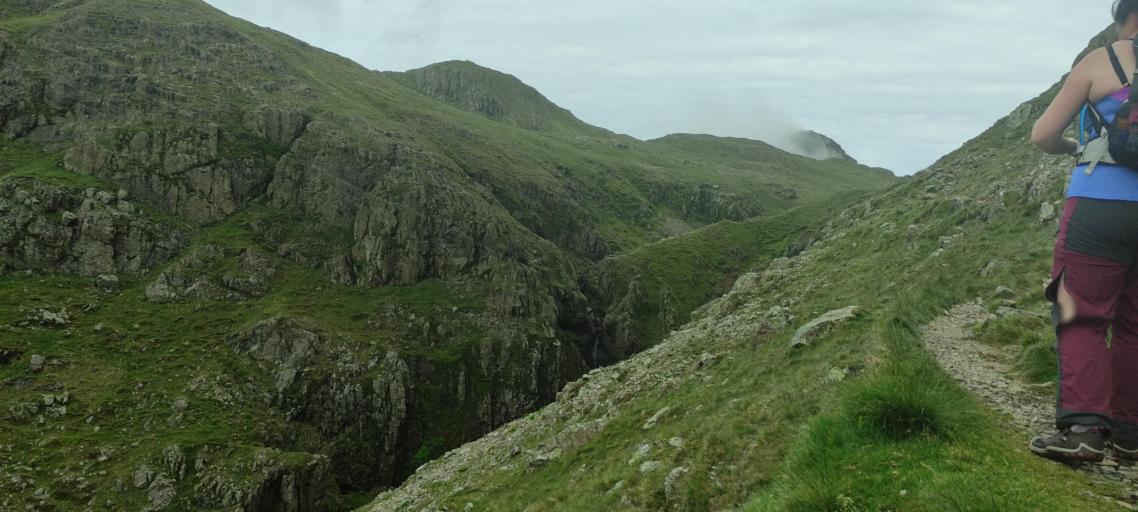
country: GB
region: England
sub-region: Cumbria
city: Keswick
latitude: 54.4553
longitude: -3.1099
